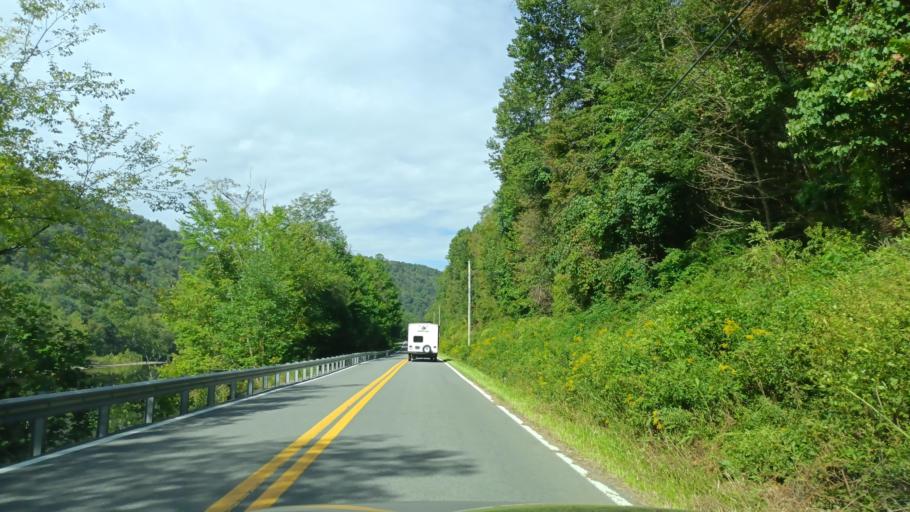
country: US
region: West Virginia
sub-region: Preston County
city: Terra Alta
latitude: 39.3105
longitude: -79.6421
